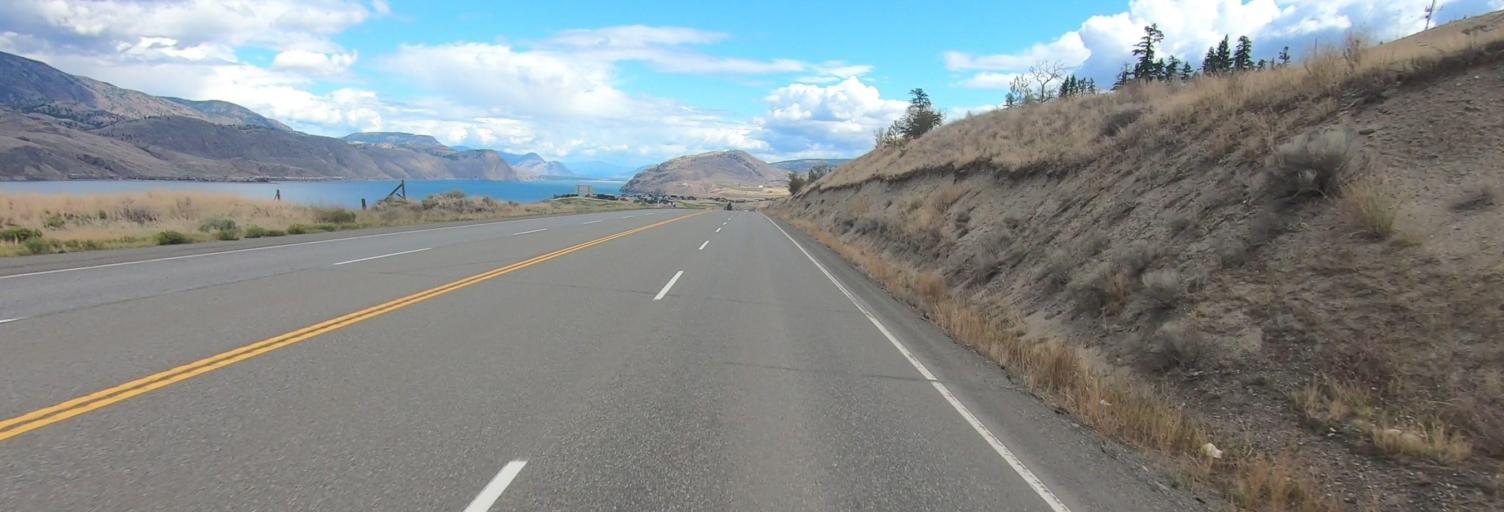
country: CA
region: British Columbia
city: Logan Lake
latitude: 50.7382
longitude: -120.7126
